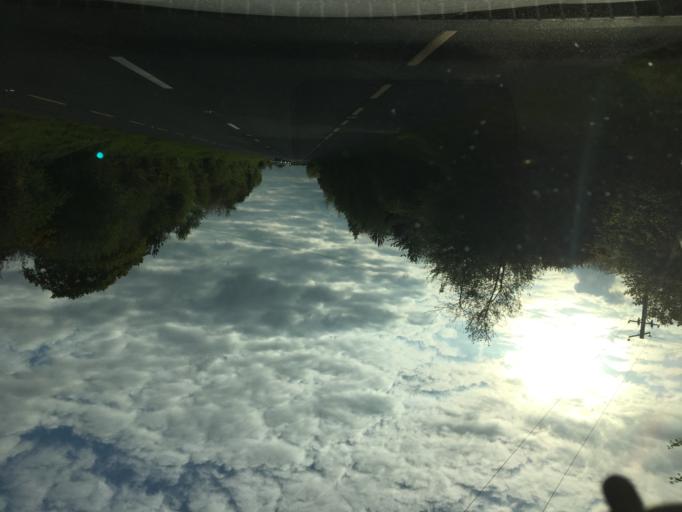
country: IE
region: Leinster
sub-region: Loch Garman
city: Enniscorthy
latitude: 52.3586
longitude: -6.7049
